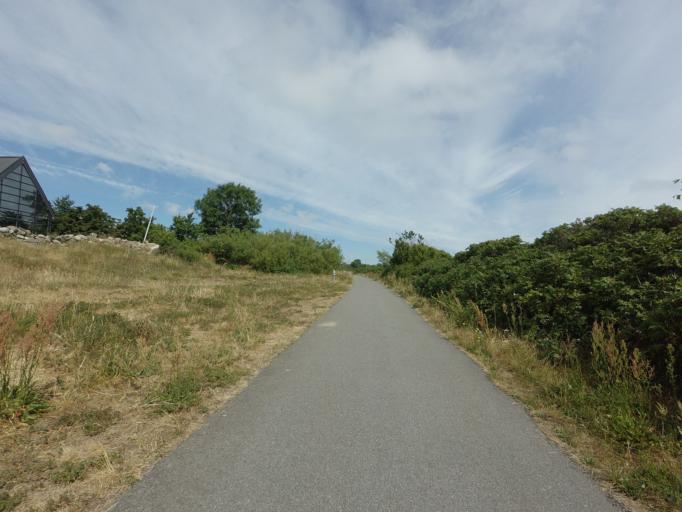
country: SE
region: Skane
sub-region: Simrishamns Kommun
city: Simrishamn
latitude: 55.5217
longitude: 14.3473
